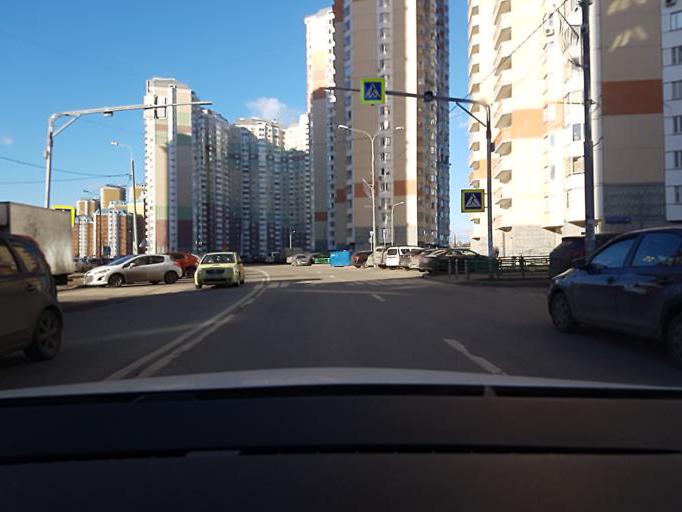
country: RU
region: Moskovskaya
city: Pavshino
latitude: 55.8216
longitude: 37.3762
